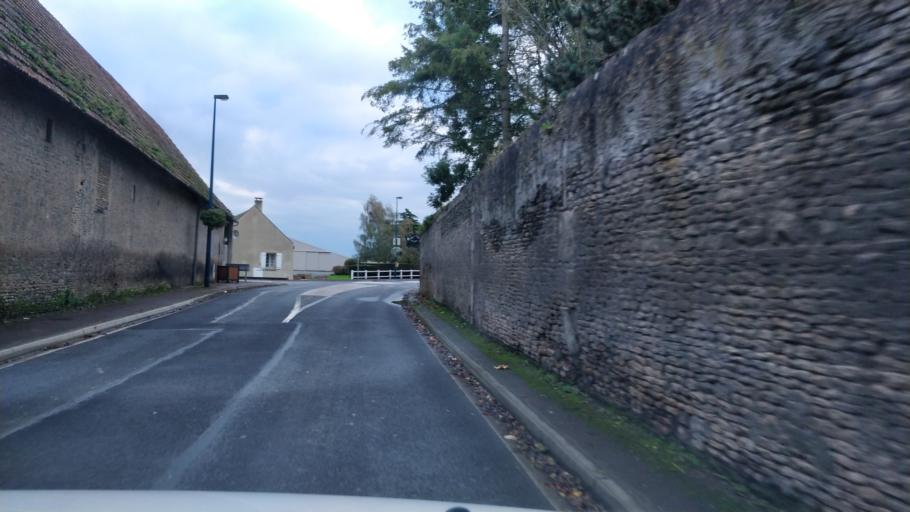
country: FR
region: Lower Normandy
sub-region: Departement du Calvados
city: Benouville
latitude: 49.2596
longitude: -0.2853
